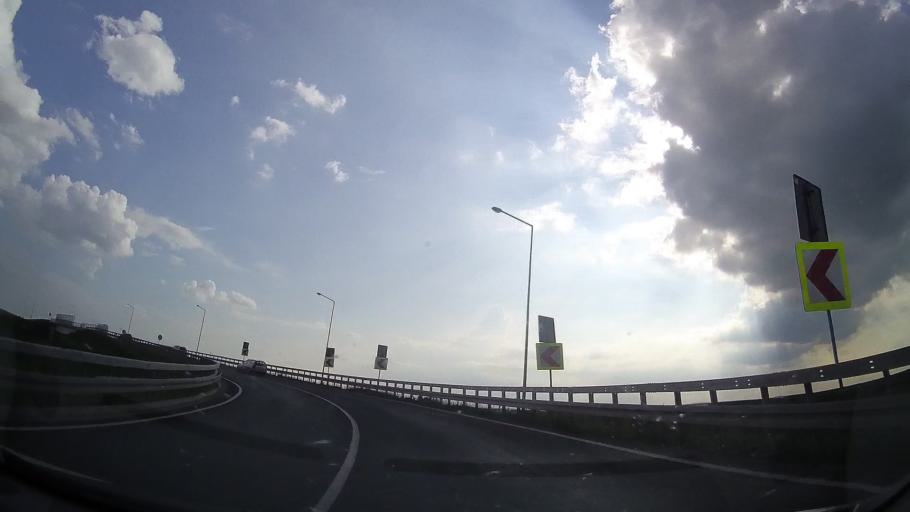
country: RO
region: Timis
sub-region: Comuna Remetea Mare
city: Remetea Mare
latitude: 45.8057
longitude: 21.4101
